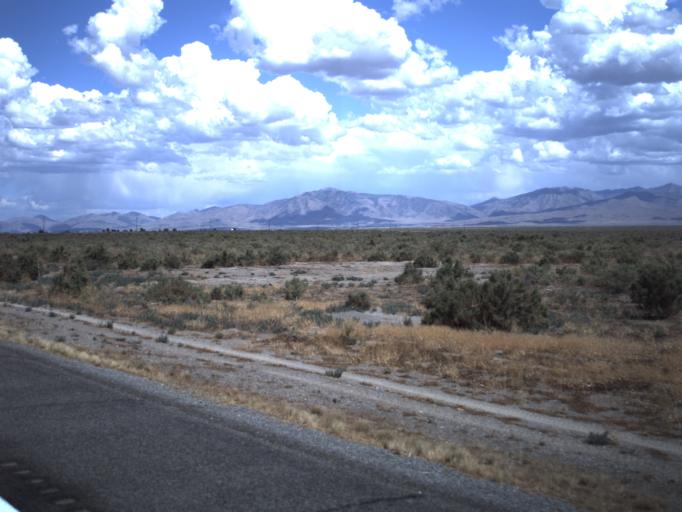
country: US
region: Utah
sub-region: Millard County
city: Delta
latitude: 39.3659
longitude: -112.5468
